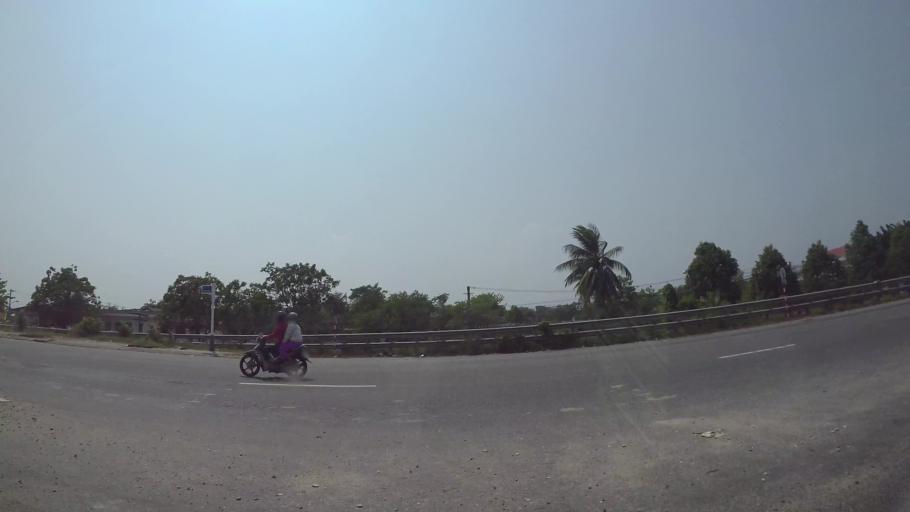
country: VN
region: Da Nang
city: Cam Le
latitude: 16.0024
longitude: 108.1903
